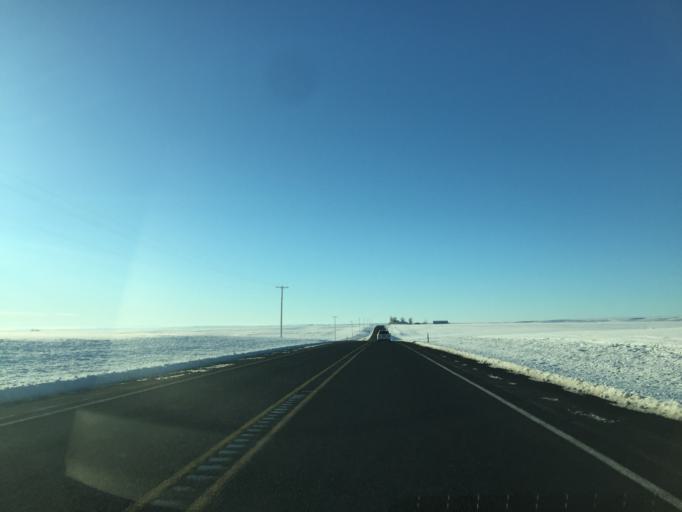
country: US
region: Washington
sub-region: Okanogan County
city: Coulee Dam
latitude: 47.6845
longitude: -119.0062
